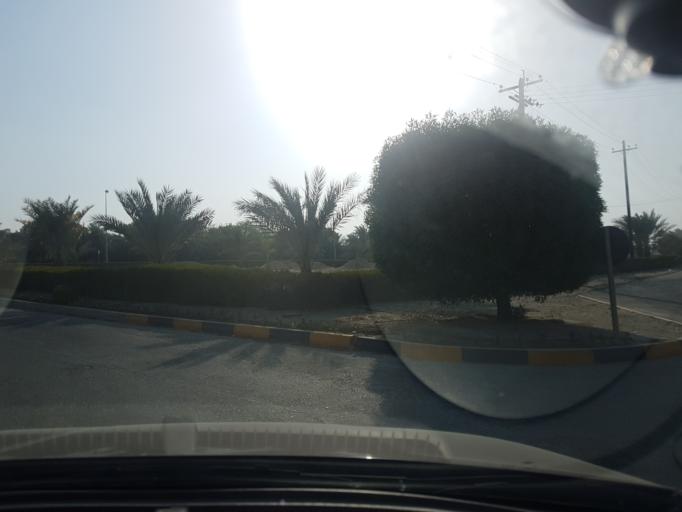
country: BH
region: Northern
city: Ar Rifa'
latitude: 26.0892
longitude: 50.5499
